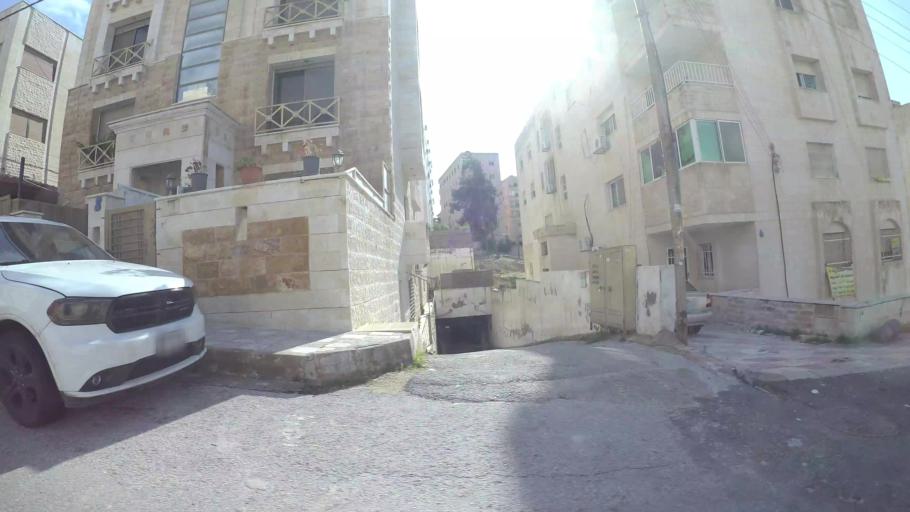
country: JO
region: Amman
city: Al Jubayhah
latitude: 32.0190
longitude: 35.8618
